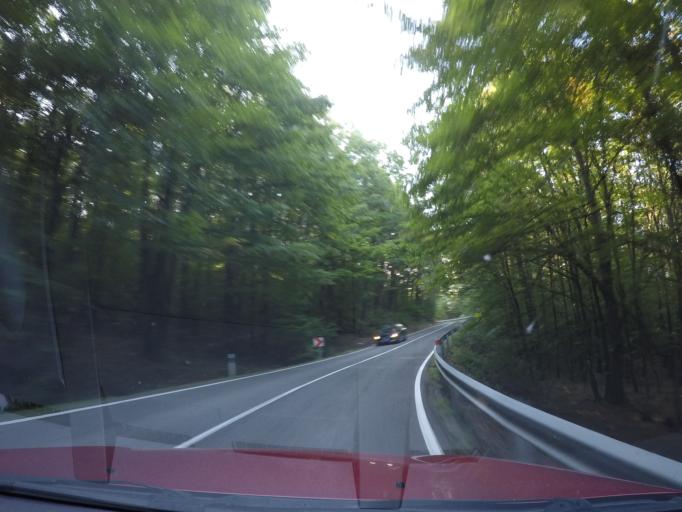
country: SK
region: Kosicky
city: Kosice
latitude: 48.7117
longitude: 21.1940
